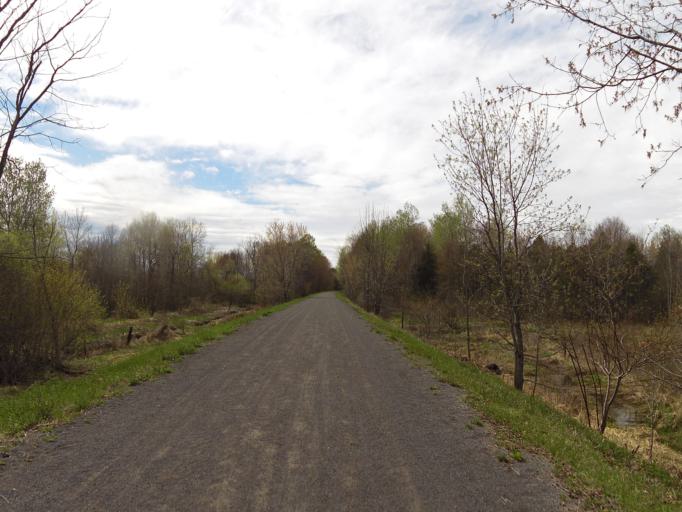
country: CA
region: Ontario
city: Hawkesbury
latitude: 45.5321
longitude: -74.6747
